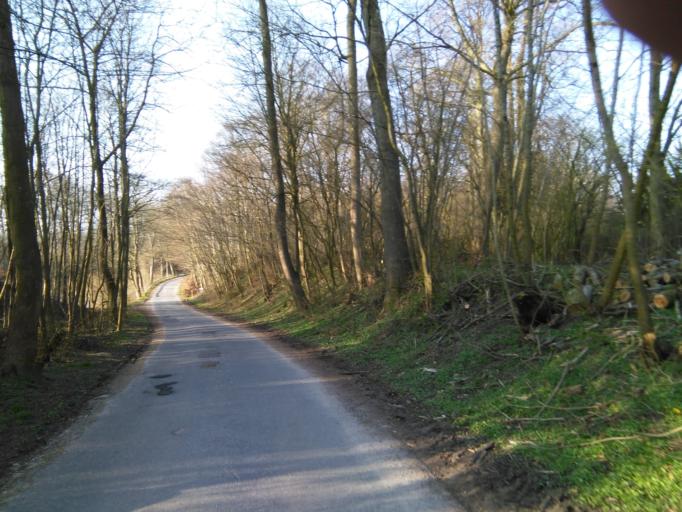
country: DK
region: Central Jutland
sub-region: Arhus Kommune
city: Beder
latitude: 56.0674
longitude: 10.1876
